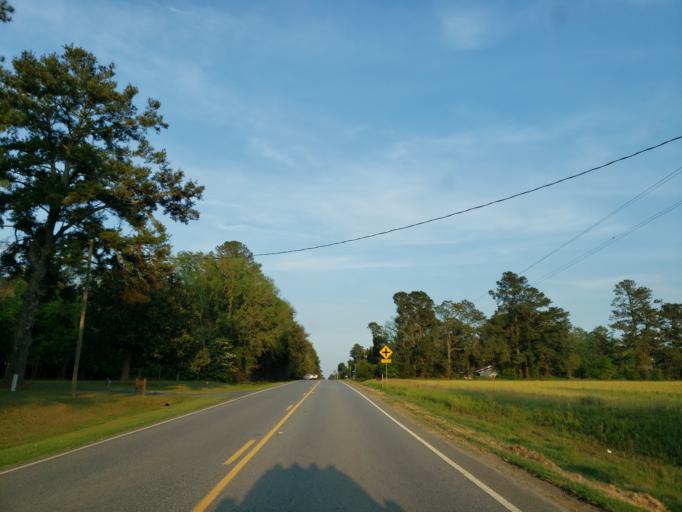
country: US
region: Georgia
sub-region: Lowndes County
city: Hahira
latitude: 30.9957
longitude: -83.4323
